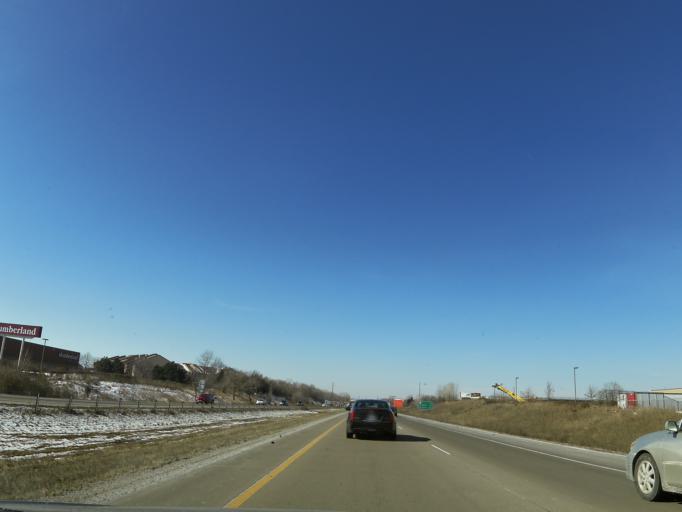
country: US
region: Minnesota
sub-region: Ramsey County
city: North Saint Paul
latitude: 45.0373
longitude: -93.0259
